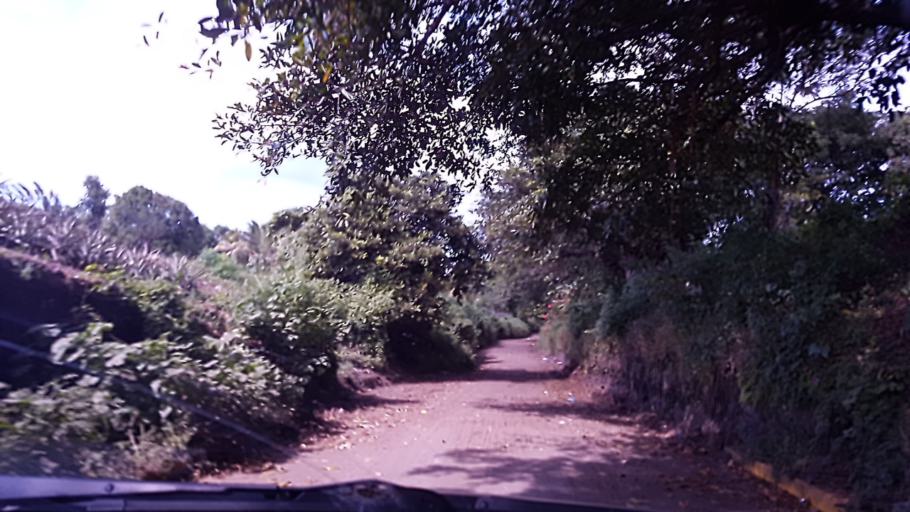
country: NI
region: Masaya
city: Ticuantepe
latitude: 11.9906
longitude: -86.2249
